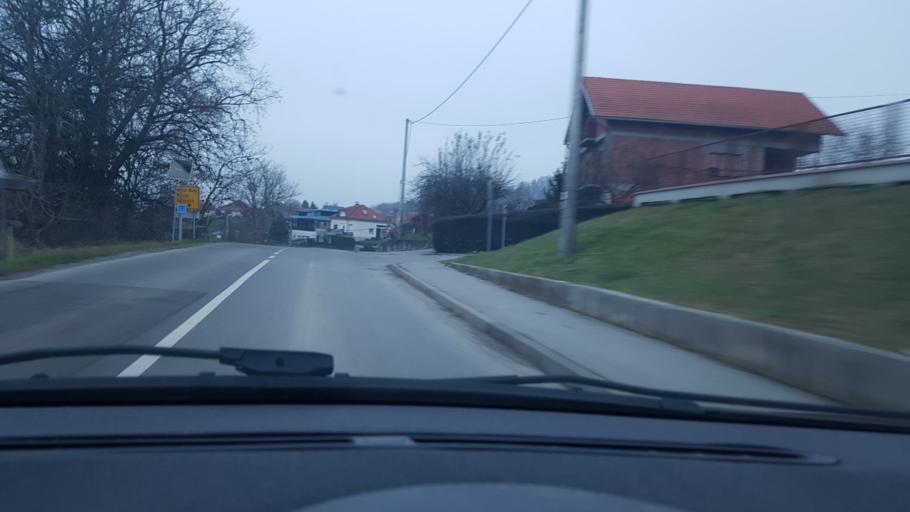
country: HR
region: Krapinsko-Zagorska
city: Zabok
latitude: 46.0719
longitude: 15.9230
